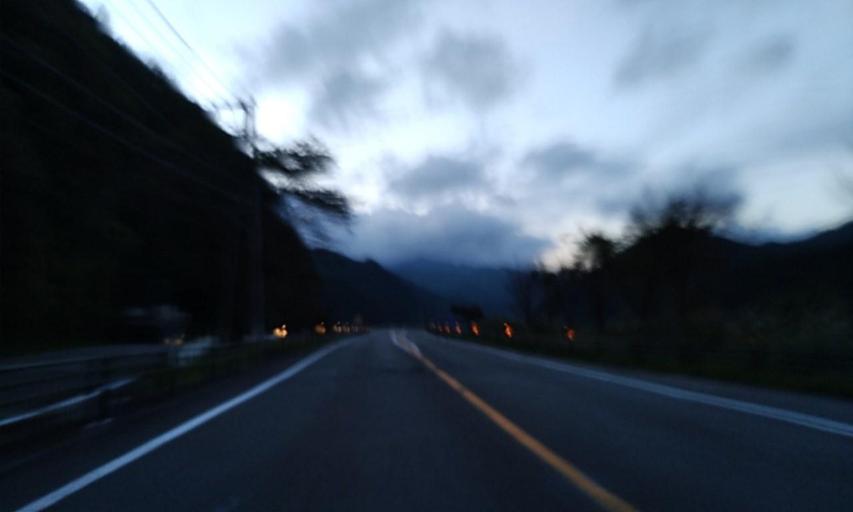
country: JP
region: Wakayama
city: Shingu
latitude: 33.7241
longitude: 135.9618
